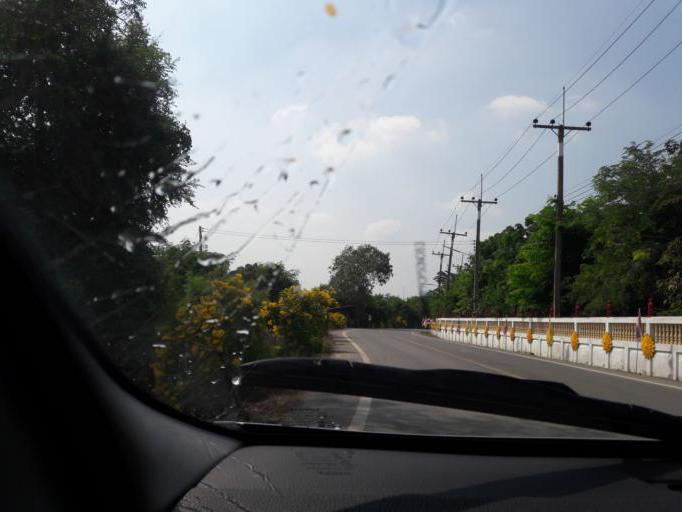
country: TH
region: Ang Thong
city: Ang Thong
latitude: 14.5712
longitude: 100.4222
